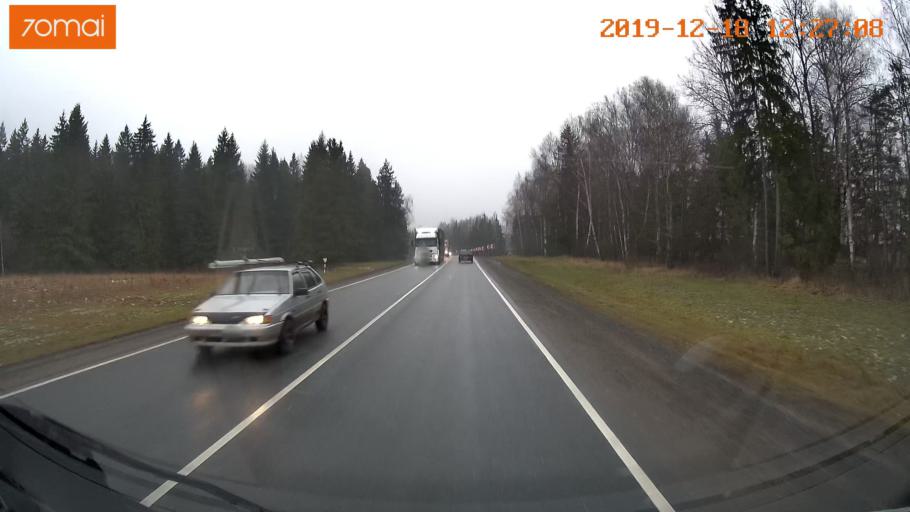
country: RU
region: Moskovskaya
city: Novopetrovskoye
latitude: 56.0591
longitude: 36.5031
